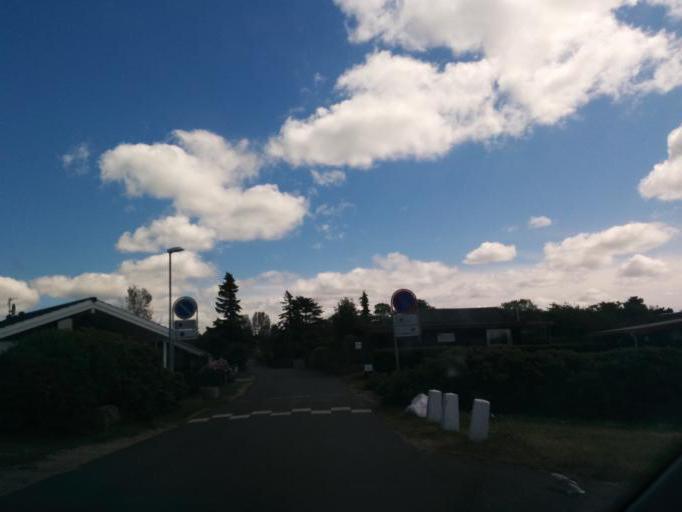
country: DK
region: Central Jutland
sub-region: Syddjurs Kommune
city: Ronde
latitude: 56.2959
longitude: 10.4338
